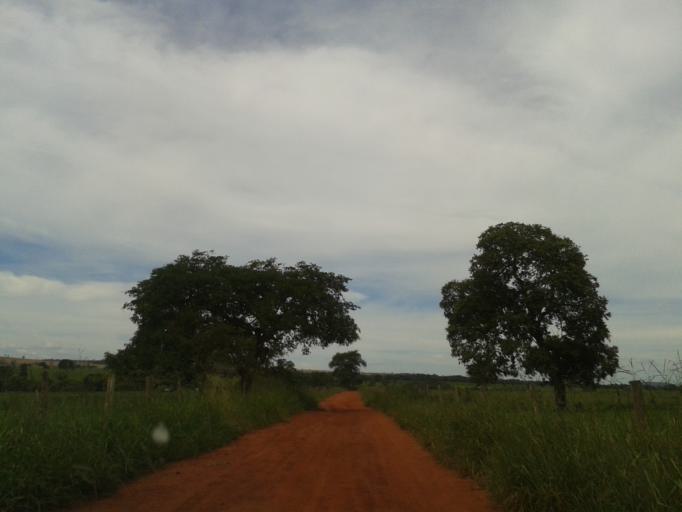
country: BR
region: Minas Gerais
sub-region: Capinopolis
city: Capinopolis
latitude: -18.7928
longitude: -49.8037
